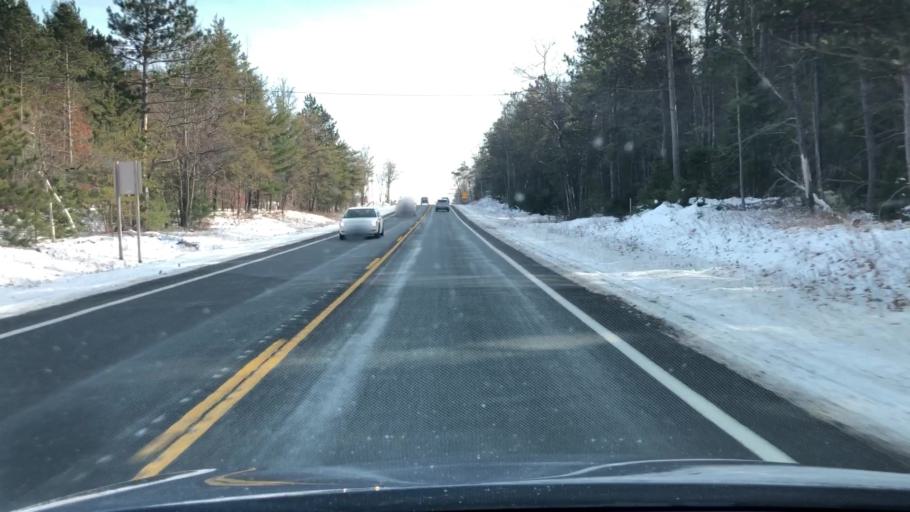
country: US
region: Michigan
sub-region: Crawford County
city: Grayling
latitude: 44.7092
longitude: -84.9355
